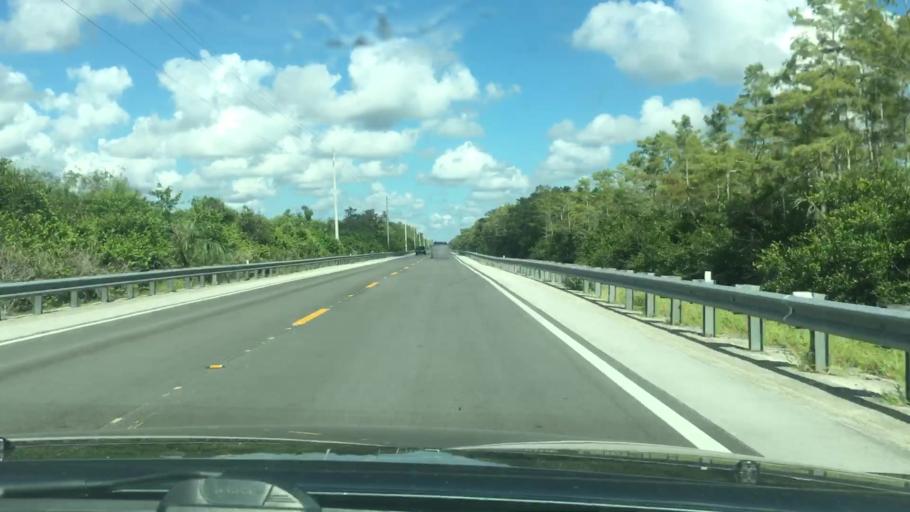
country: US
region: Florida
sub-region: Miami-Dade County
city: Kendall West
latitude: 25.7653
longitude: -80.8318
